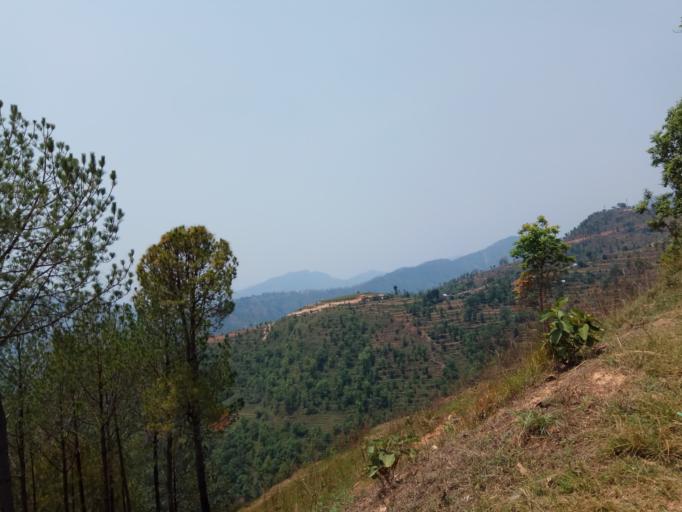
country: NP
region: Central Region
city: Kirtipur
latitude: 27.8928
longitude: 85.0790
